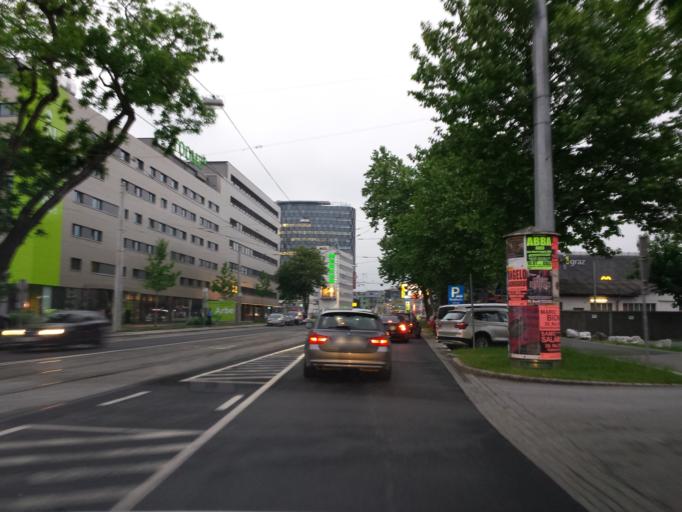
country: AT
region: Styria
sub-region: Graz Stadt
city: Graz
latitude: 47.0545
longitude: 15.4485
